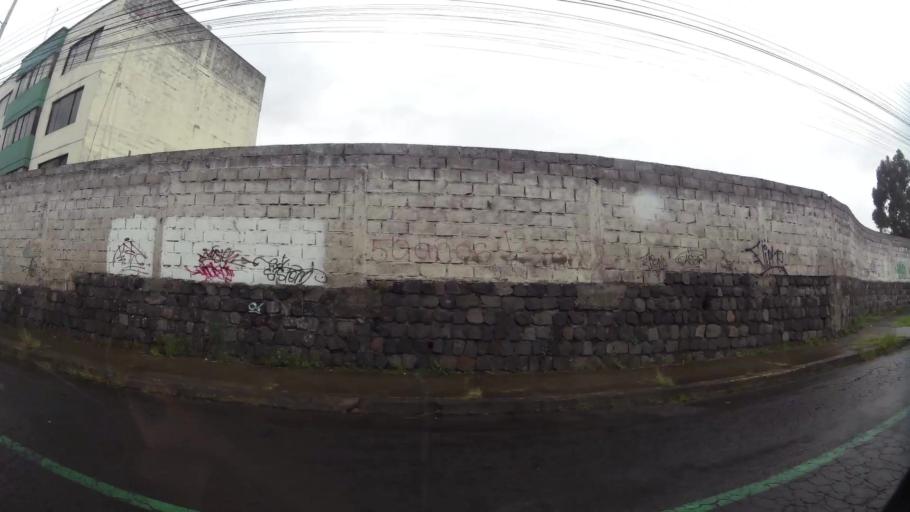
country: EC
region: Pichincha
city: Sangolqui
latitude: -0.3184
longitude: -78.4423
